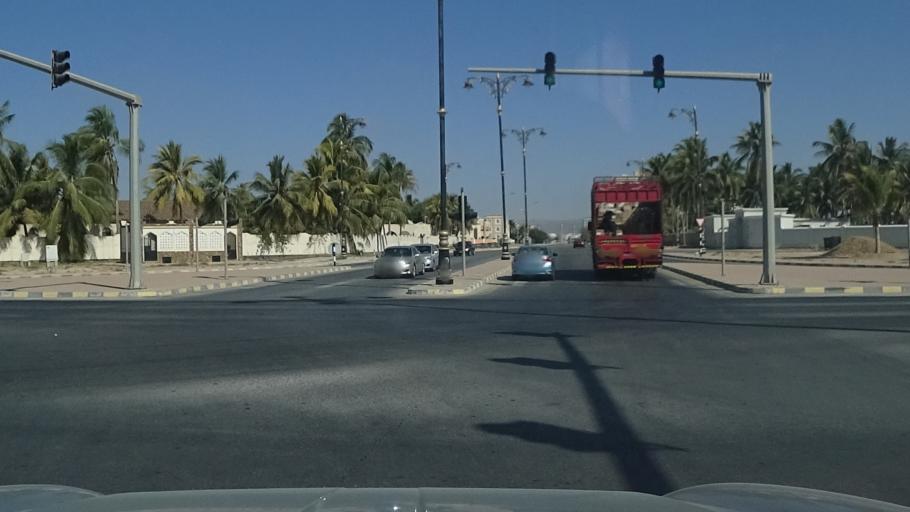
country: OM
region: Zufar
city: Salalah
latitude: 17.0360
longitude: 54.1606
